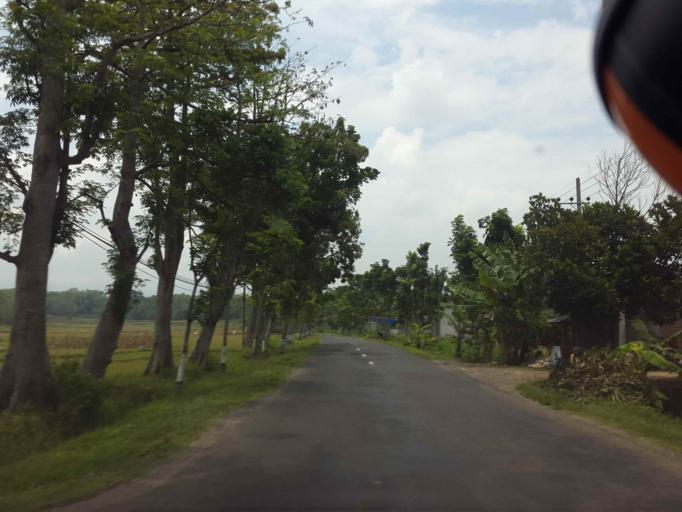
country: ID
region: East Java
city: Madiun
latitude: -7.7092
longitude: 111.3524
